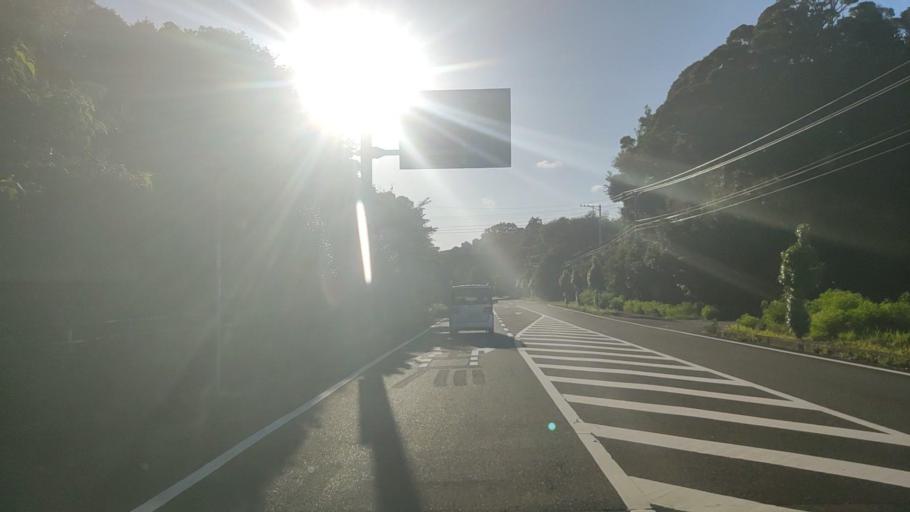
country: JP
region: Mie
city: Toba
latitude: 34.2678
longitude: 136.8096
